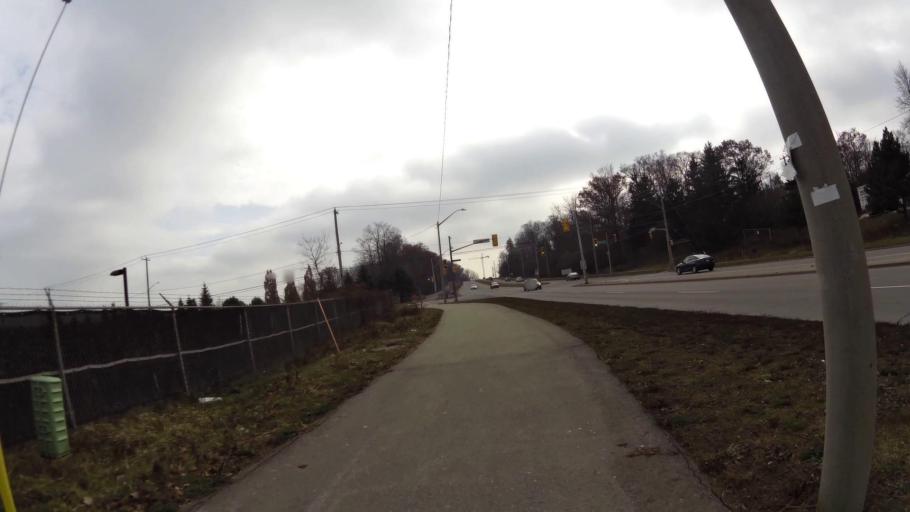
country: CA
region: Ontario
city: Kitchener
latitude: 43.4241
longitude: -80.4762
